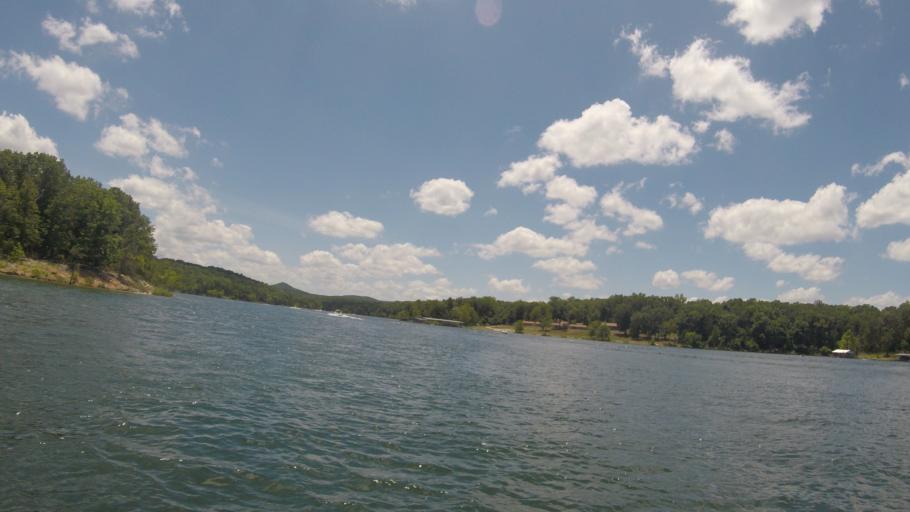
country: US
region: Missouri
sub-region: Barry County
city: Shell Knob
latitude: 36.5831
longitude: -93.5671
